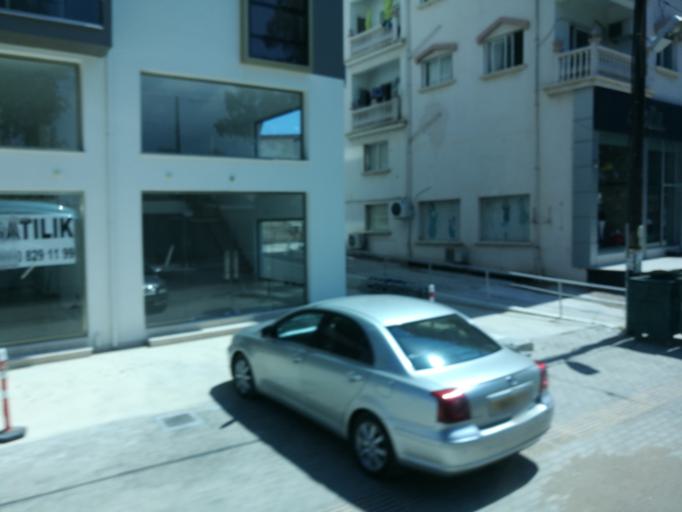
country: CY
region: Ammochostos
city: Famagusta
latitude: 35.1386
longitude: 33.9176
